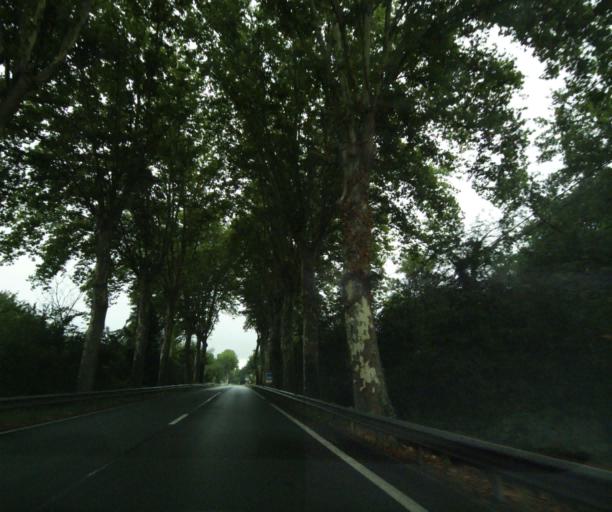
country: FR
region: Midi-Pyrenees
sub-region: Departement du Tarn
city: Le Garric
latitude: 43.9759
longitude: 2.1789
